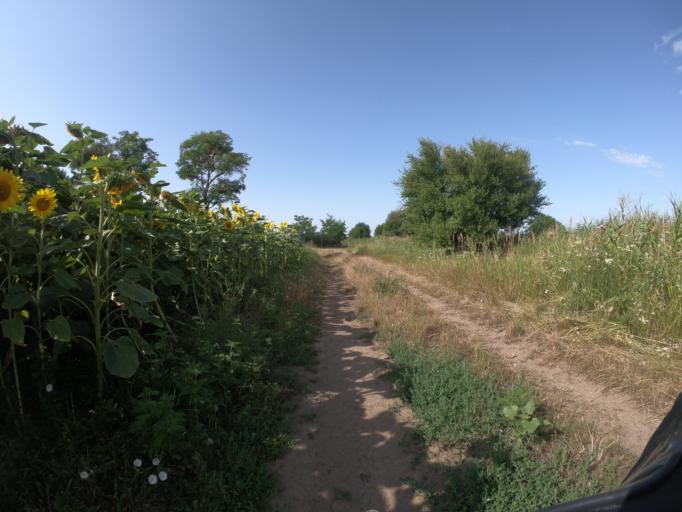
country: HU
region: Hajdu-Bihar
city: Egyek
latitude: 47.5831
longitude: 20.9595
